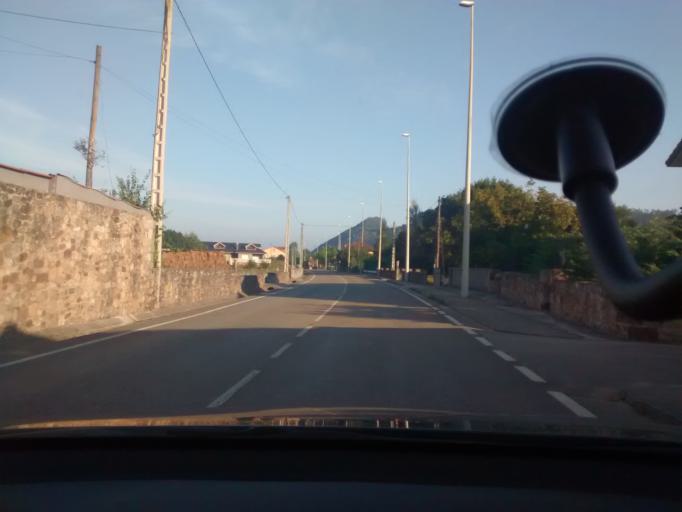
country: ES
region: Cantabria
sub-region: Provincia de Cantabria
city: Entrambasaguas
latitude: 43.3709
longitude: -3.7155
